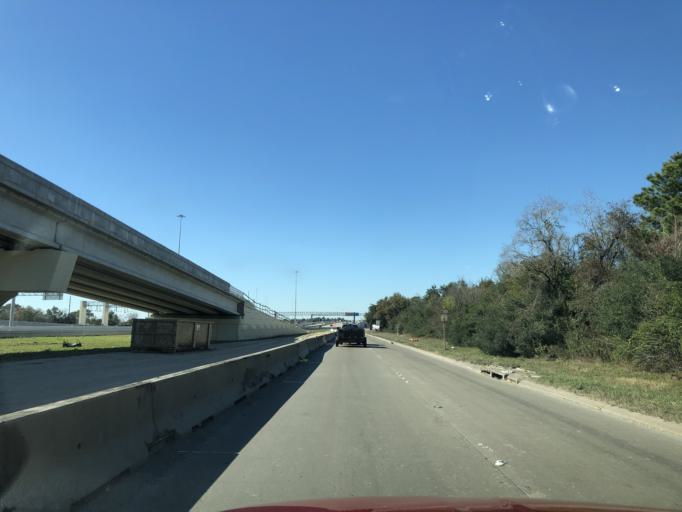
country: US
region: Texas
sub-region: Brazoria County
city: Brookside Village
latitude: 29.5977
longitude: -95.3924
